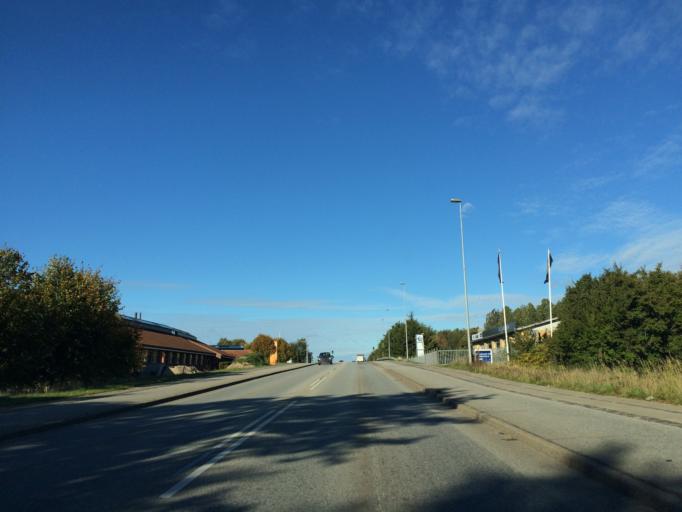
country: DK
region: Central Jutland
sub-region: Randers Kommune
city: Randers
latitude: 56.4496
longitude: 10.0590
